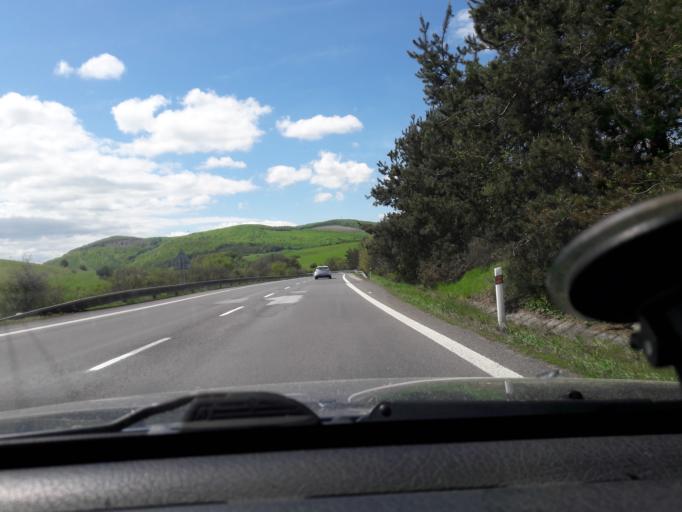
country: SK
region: Banskobystricky
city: Krupina
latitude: 48.4279
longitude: 19.0933
